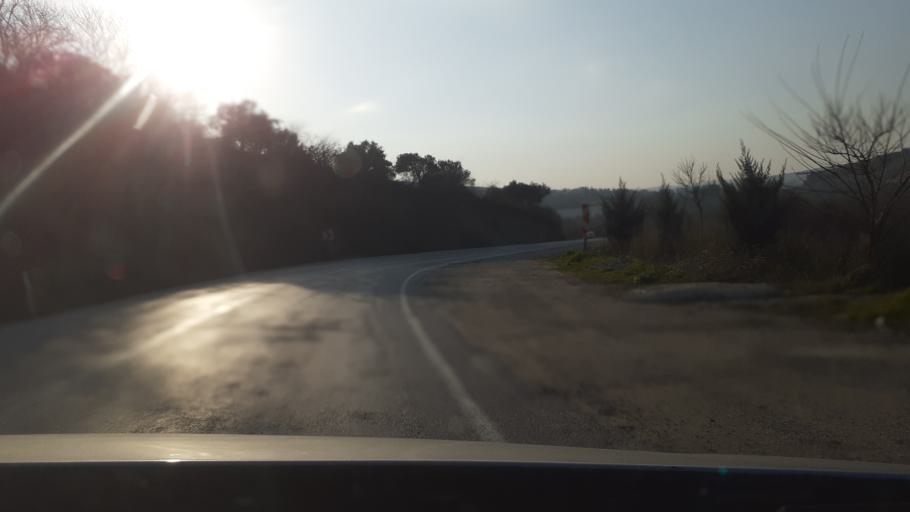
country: TR
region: Hatay
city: Oymakli
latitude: 36.1108
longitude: 36.2776
